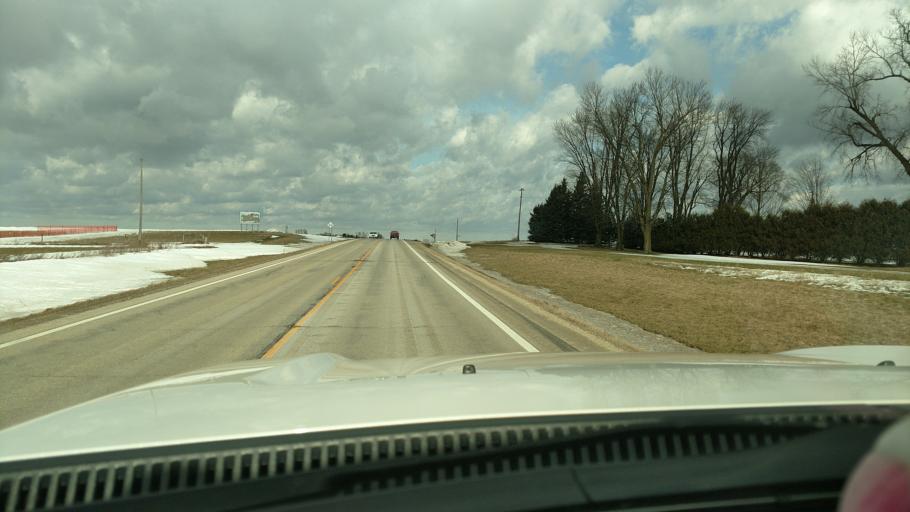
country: US
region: Minnesota
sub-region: Wabasha County
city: Wabasha
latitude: 44.2498
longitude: -92.0553
